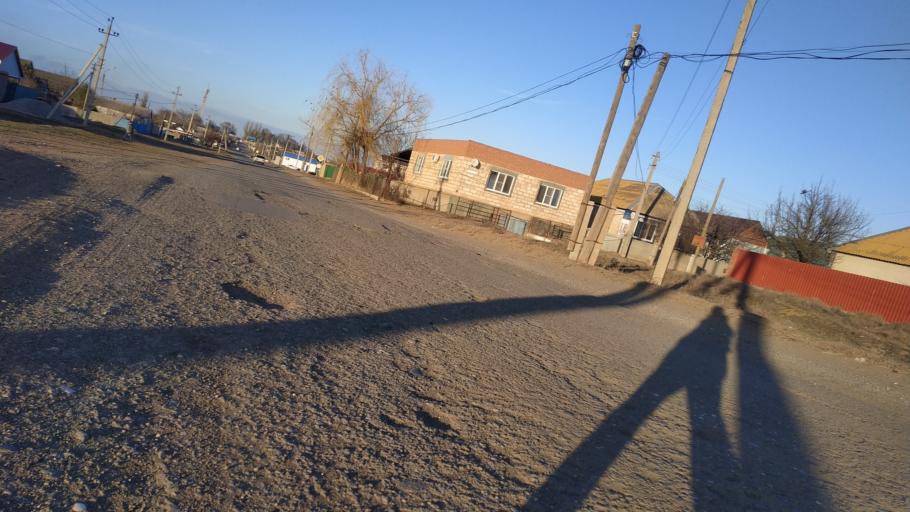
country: RU
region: Astrakhan
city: Liman
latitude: 45.7830
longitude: 47.2091
